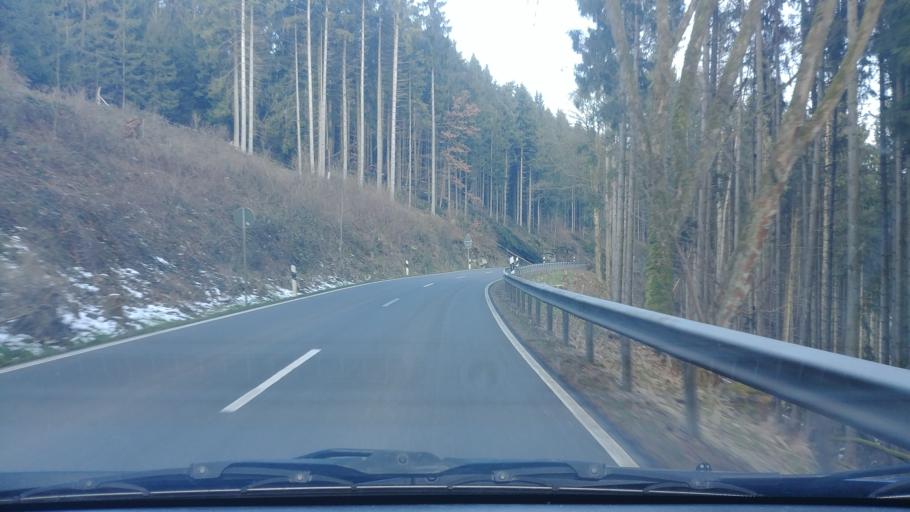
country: DE
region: Lower Saxony
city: Dassel
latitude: 51.7629
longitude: 9.6834
